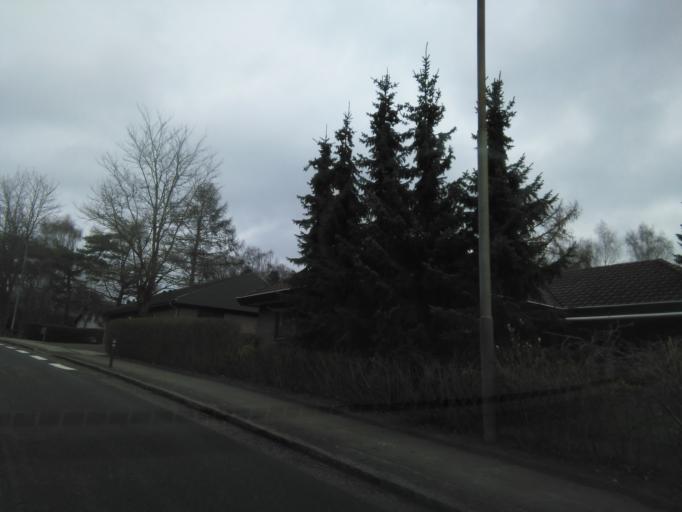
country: DK
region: Central Jutland
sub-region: Arhus Kommune
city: Stavtrup
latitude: 56.1608
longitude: 10.1023
